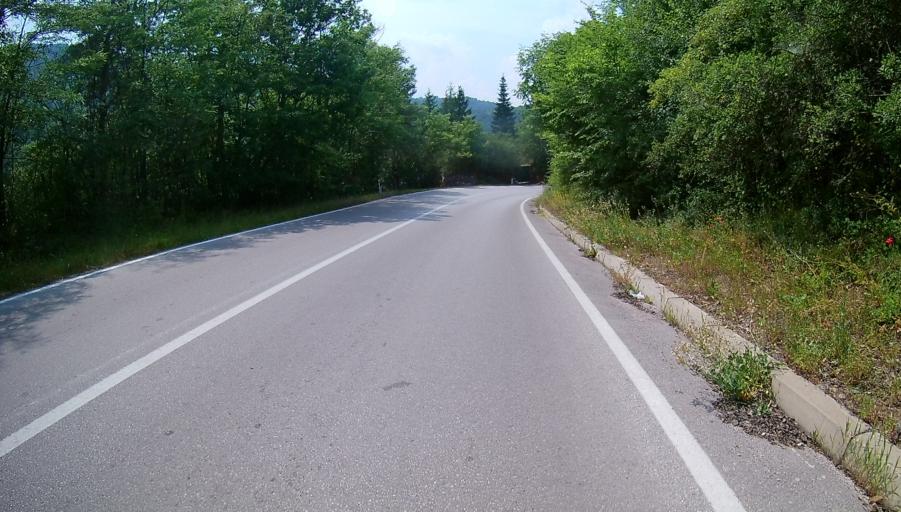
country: RS
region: Central Serbia
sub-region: Nisavski Okrug
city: Gadzin Han
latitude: 43.1829
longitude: 22.0244
